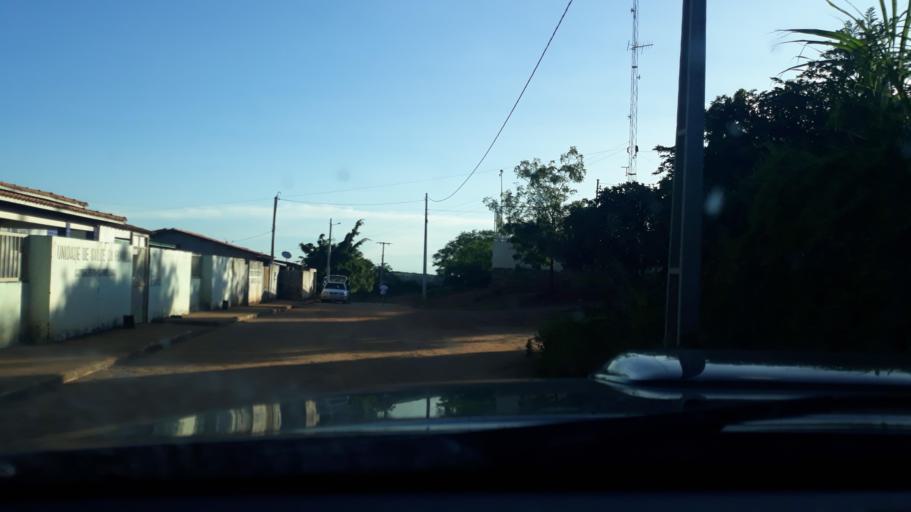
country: BR
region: Bahia
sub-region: Riacho De Santana
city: Riacho de Santana
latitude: -13.8255
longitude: -42.7270
